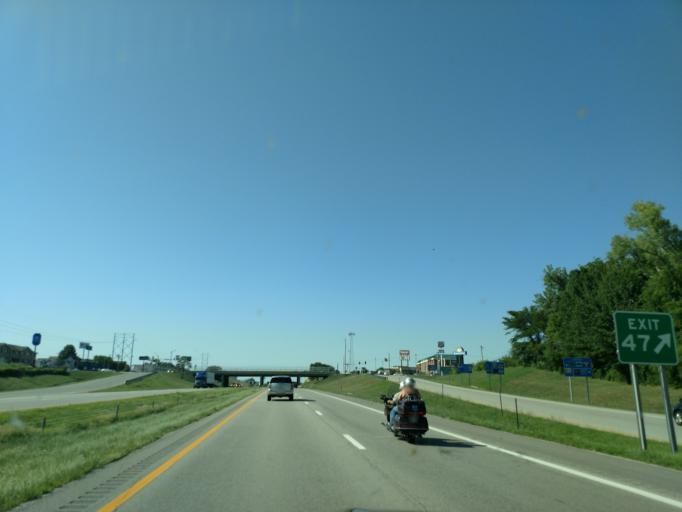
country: US
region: Missouri
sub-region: Buchanan County
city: Saint Joseph
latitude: 39.7747
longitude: -94.7933
